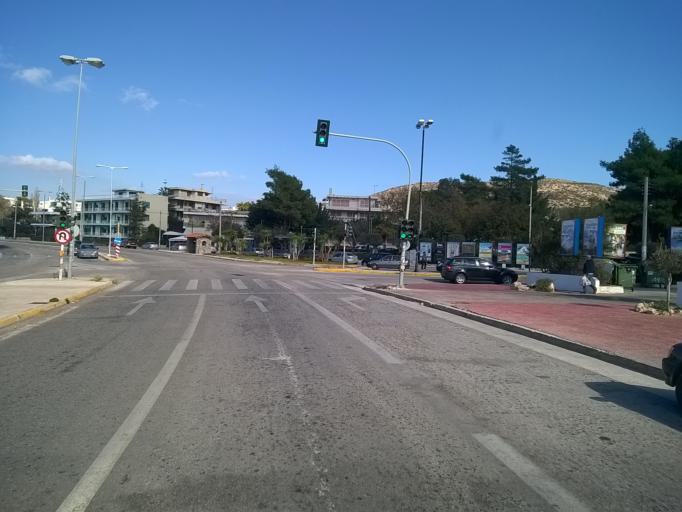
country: GR
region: Attica
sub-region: Nomarchia Anatolikis Attikis
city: Saronida
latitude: 37.7487
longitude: 23.9057
